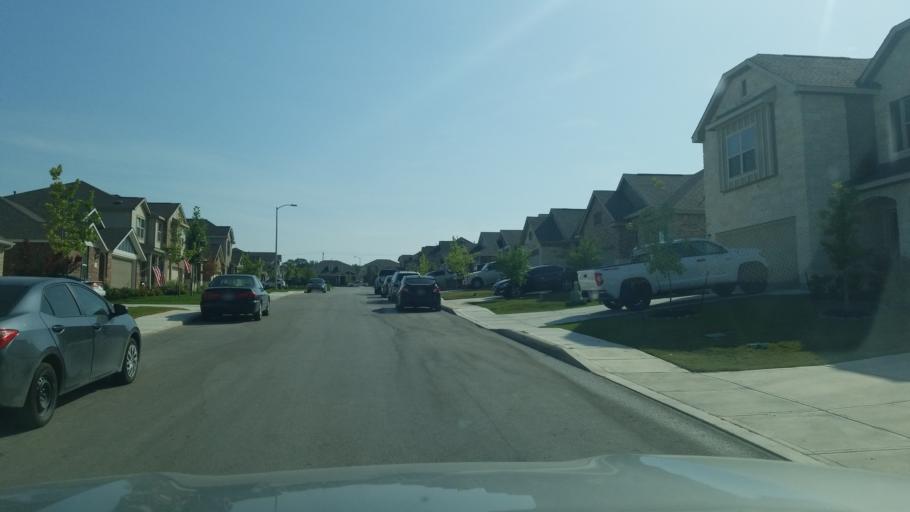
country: US
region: Texas
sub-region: Medina County
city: La Coste
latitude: 29.4055
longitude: -98.7861
